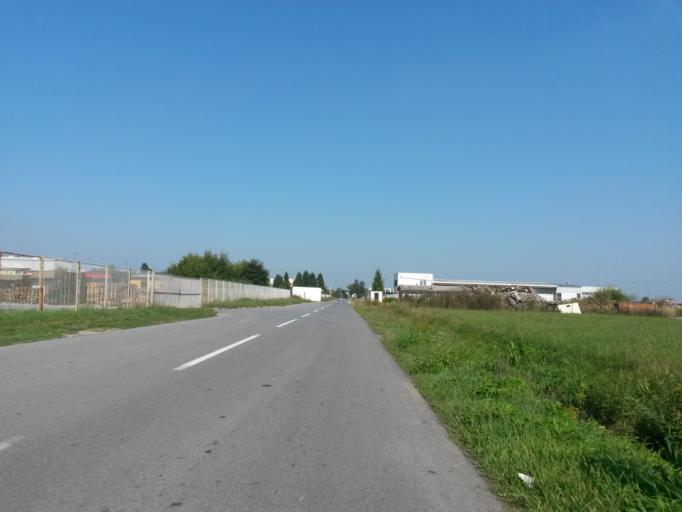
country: HR
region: Osjecko-Baranjska
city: Brijest
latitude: 45.5398
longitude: 18.6529
